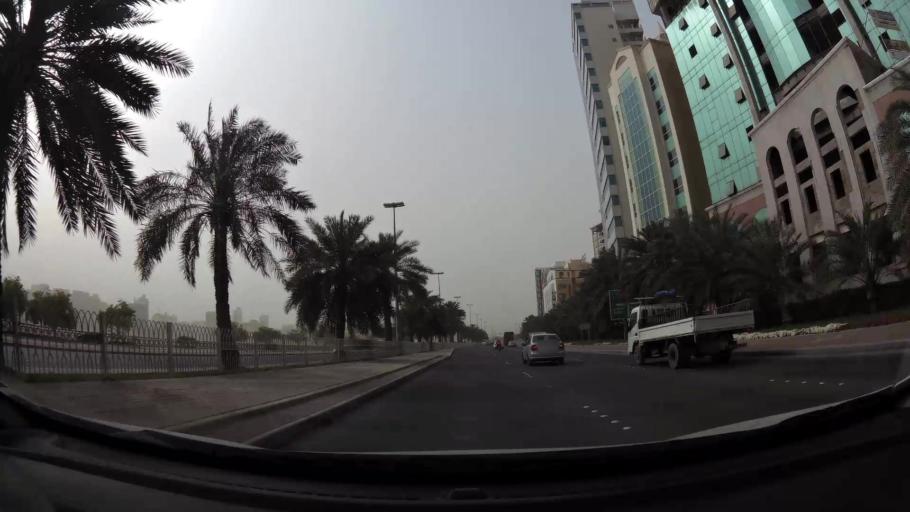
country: BH
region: Manama
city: Manama
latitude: 26.2273
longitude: 50.5986
